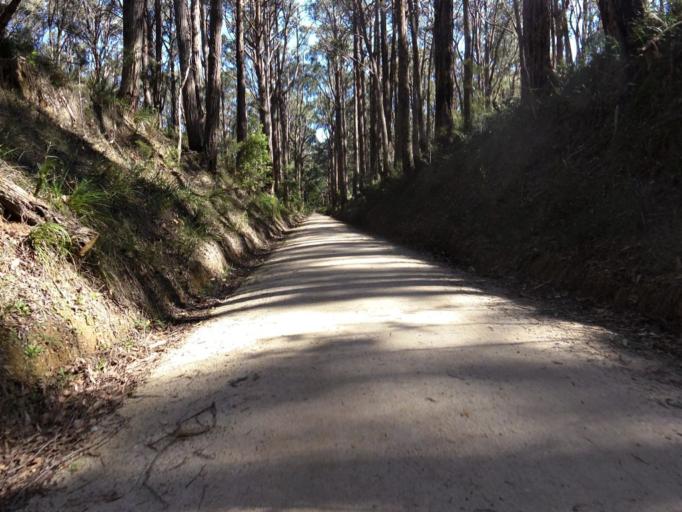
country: AU
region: Victoria
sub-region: Latrobe
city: Moe
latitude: -38.3939
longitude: 146.1786
